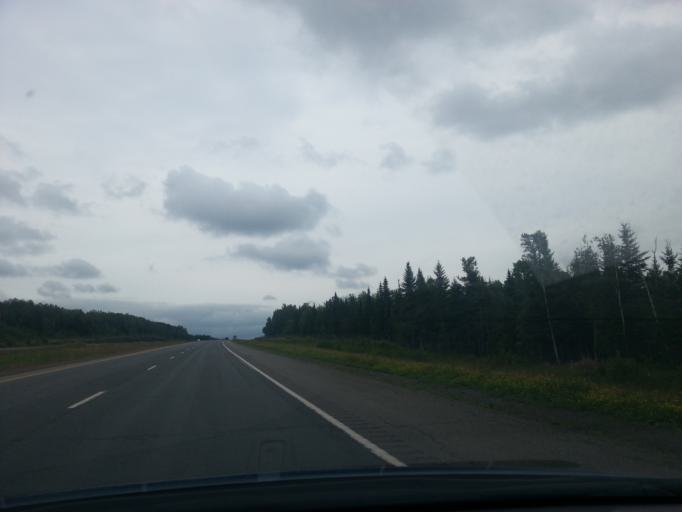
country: CA
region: New Brunswick
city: Harrison Brook
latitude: 47.3191
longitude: -68.1048
